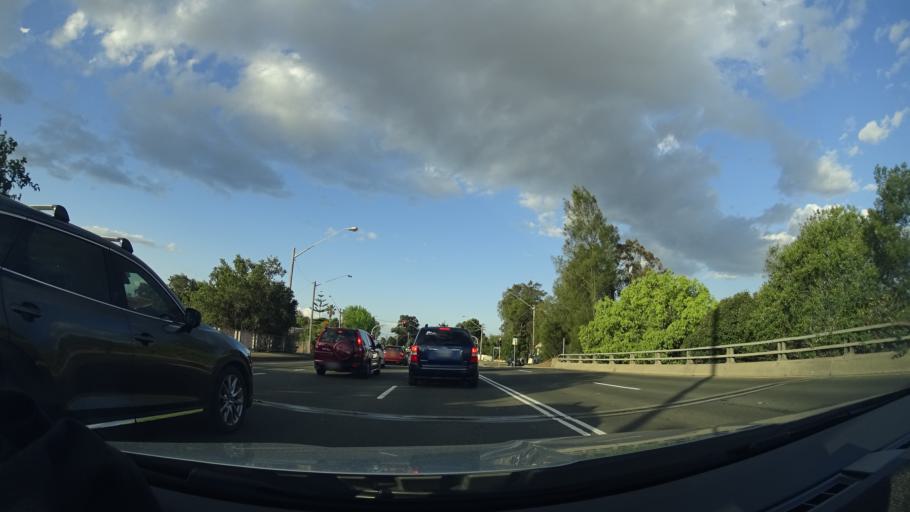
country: AU
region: New South Wales
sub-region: Canterbury
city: Belfield
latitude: -33.9068
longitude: 151.0781
